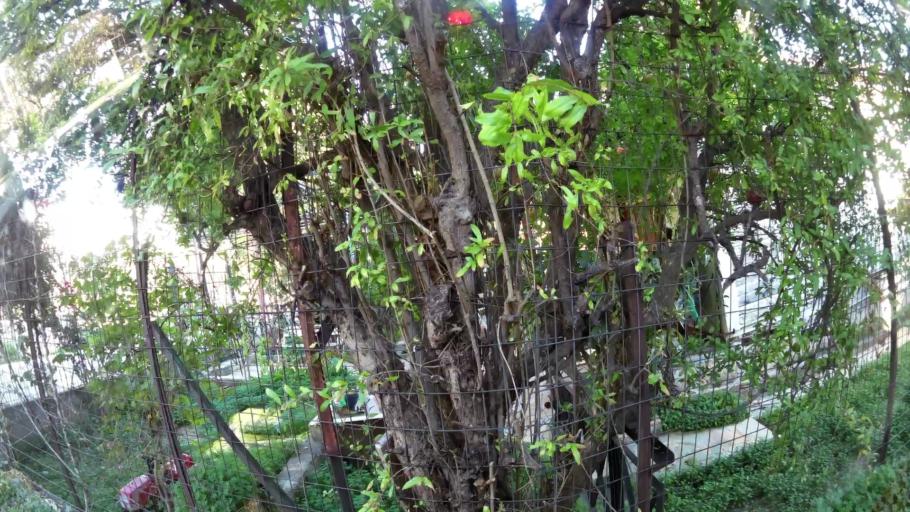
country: GR
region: Attica
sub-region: Nomarchia Anatolikis Attikis
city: Rafina
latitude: 38.0231
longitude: 23.9995
